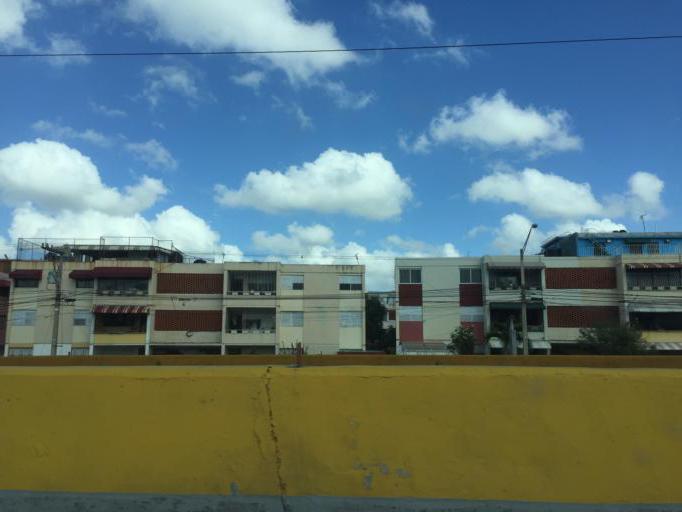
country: DO
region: Santo Domingo
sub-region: Santo Domingo
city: Santo Domingo Este
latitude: 18.4846
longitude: -69.8610
